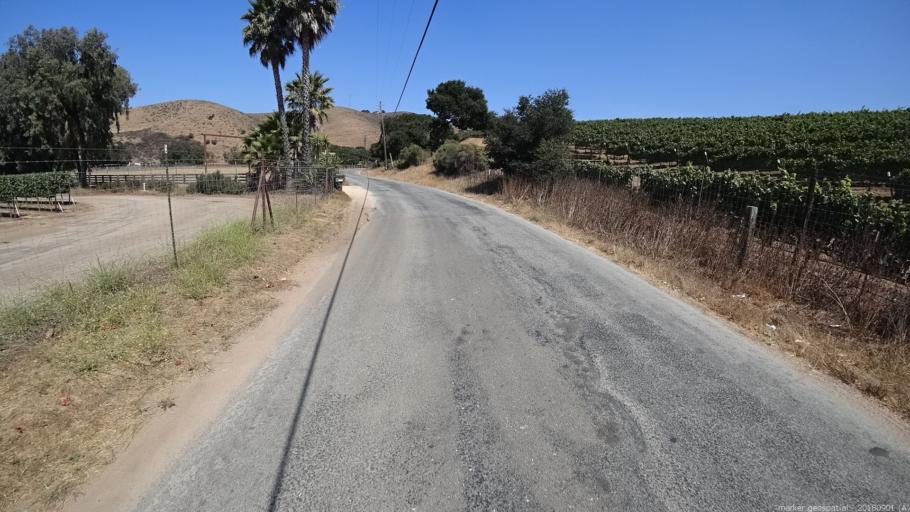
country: US
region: California
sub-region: Monterey County
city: Chualar
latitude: 36.5966
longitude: -121.4382
